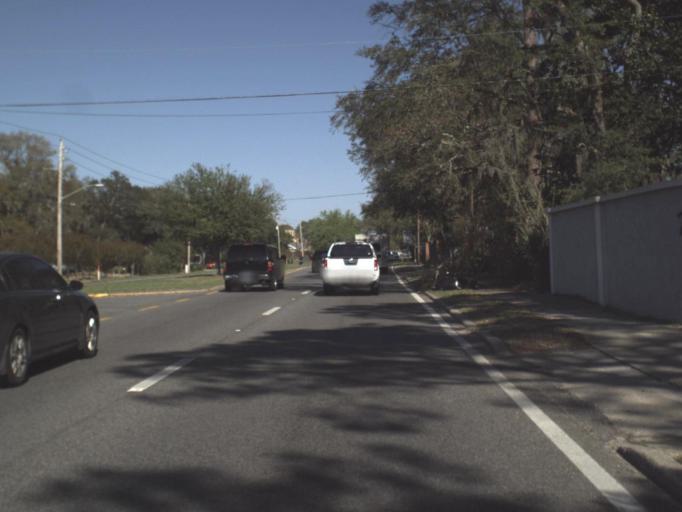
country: US
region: Florida
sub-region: Okaloosa County
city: Mary Esther
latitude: 30.4092
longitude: -86.6521
